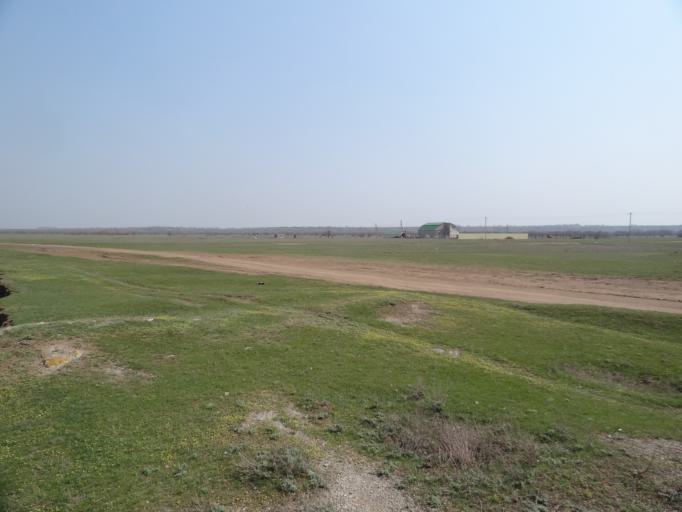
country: RU
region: Saratov
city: Privolzhskiy
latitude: 51.2645
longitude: 45.9223
